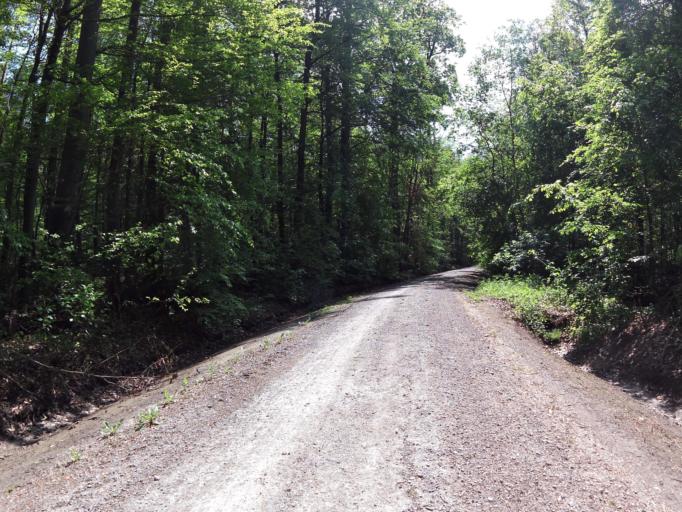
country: DE
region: Bavaria
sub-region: Regierungsbezirk Unterfranken
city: Kist
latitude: 49.7498
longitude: 9.8557
